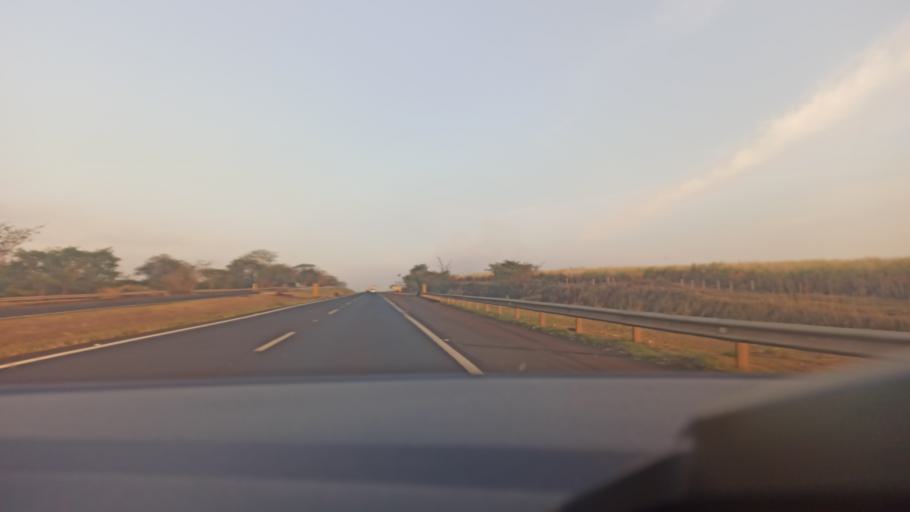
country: BR
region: Sao Paulo
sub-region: Taquaritinga
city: Taquaritinga
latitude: -21.4355
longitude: -48.6568
